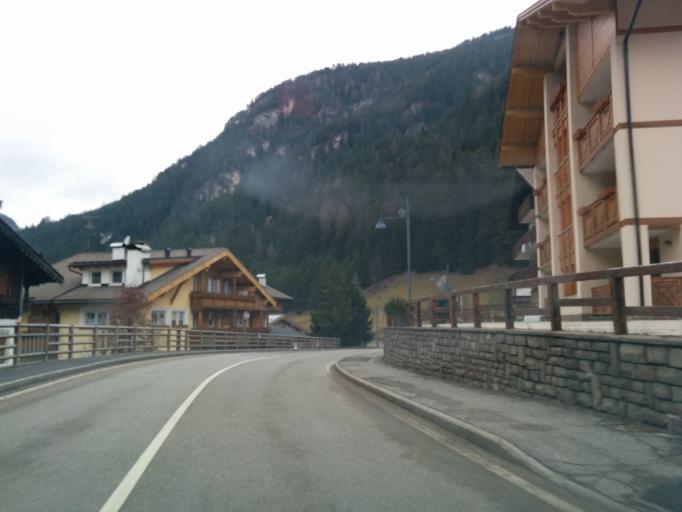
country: IT
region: Trentino-Alto Adige
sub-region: Provincia di Trento
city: Canazei
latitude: 46.4785
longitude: 11.7630
